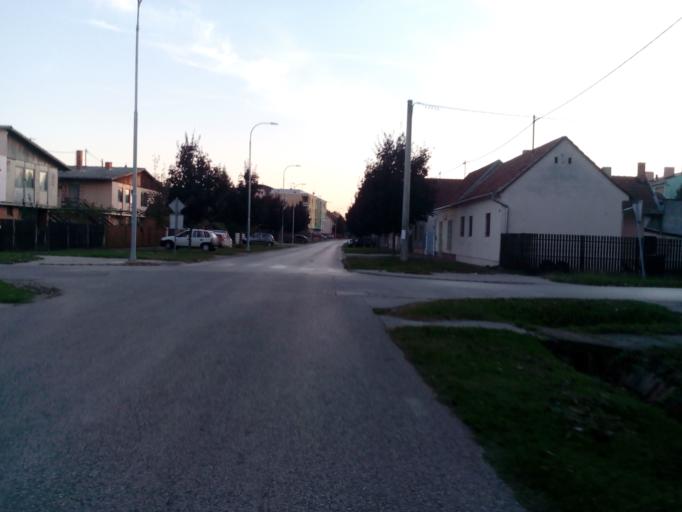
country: HR
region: Vukovarsko-Srijemska
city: Vinkovci
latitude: 45.2982
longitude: 18.8172
